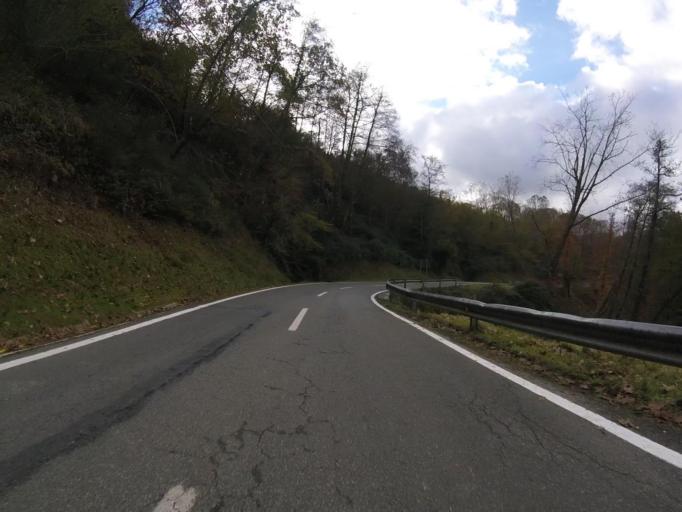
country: ES
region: Navarre
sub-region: Provincia de Navarra
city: Goizueta
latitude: 43.2053
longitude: -1.8562
